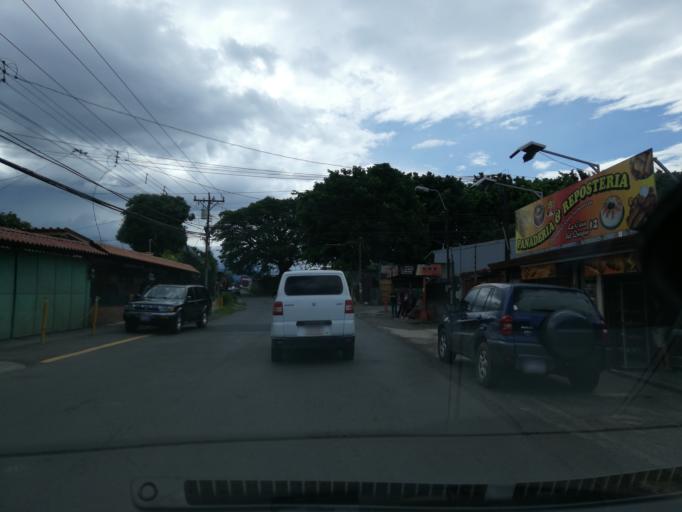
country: CR
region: Alajuela
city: Alajuela
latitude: 9.9917
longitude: -84.2363
